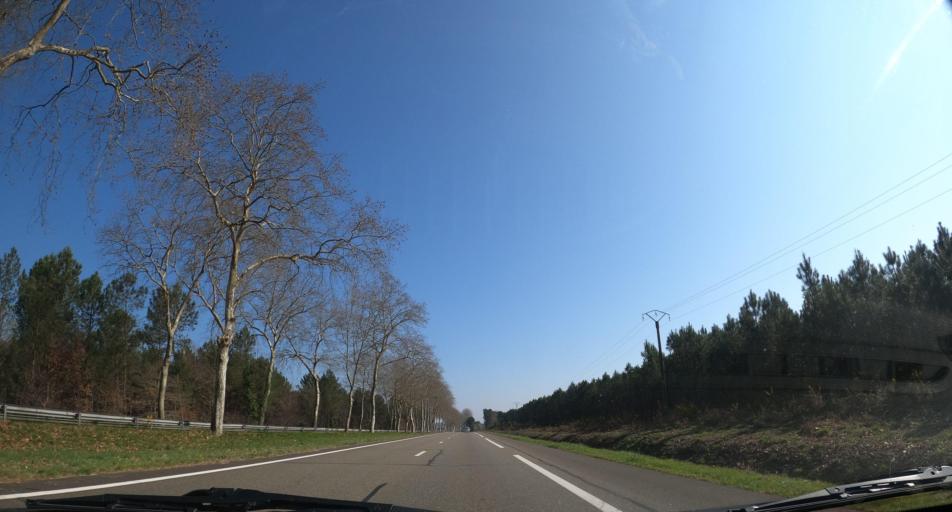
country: FR
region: Aquitaine
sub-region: Departement des Landes
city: Riviere-Saas-et-Gourby
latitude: 43.7139
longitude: -1.1441
